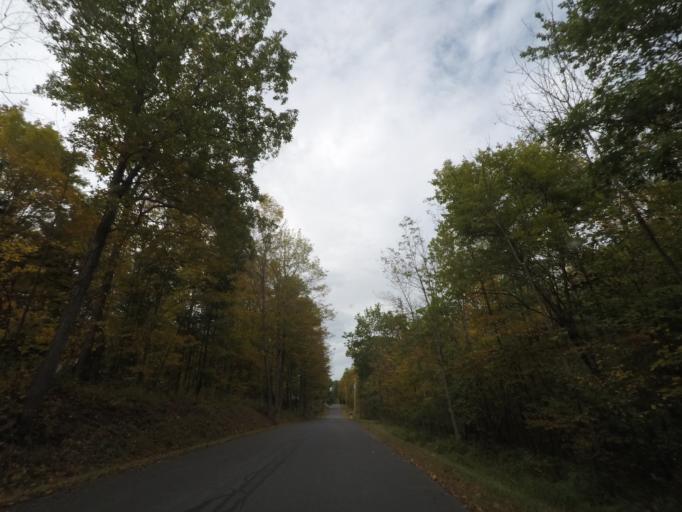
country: US
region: New York
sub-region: Rensselaer County
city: Nassau
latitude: 42.5363
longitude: -73.6456
